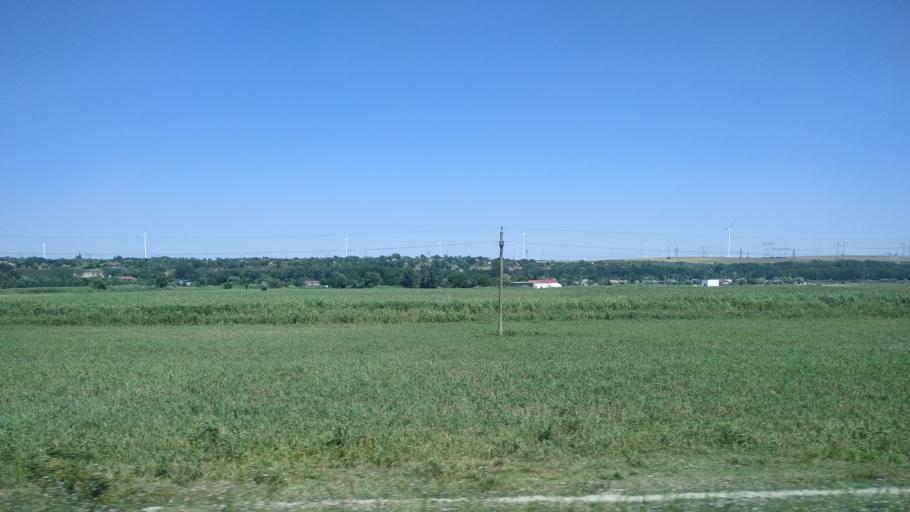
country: RO
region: Constanta
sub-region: Comuna Saligny
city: Faclia
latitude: 44.2717
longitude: 28.1094
